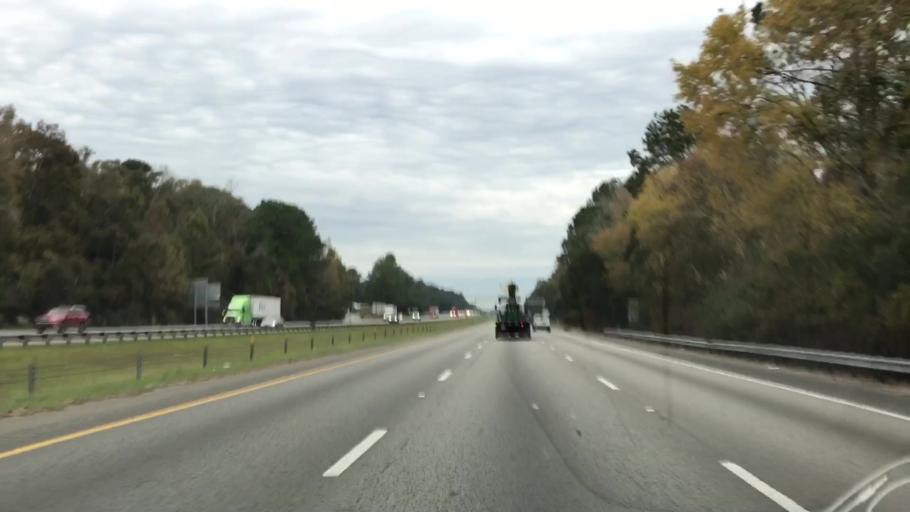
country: US
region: South Carolina
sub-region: Berkeley County
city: Ladson
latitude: 32.9870
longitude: -80.0815
